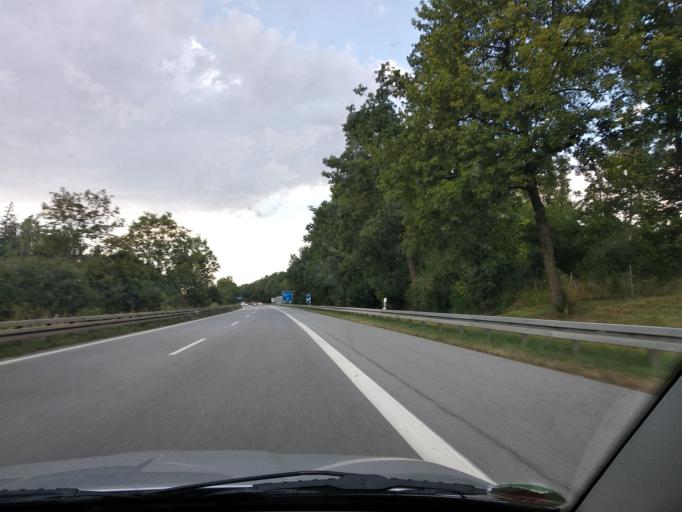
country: DE
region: Bavaria
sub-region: Upper Bavaria
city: Unterhaching
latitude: 48.0751
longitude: 11.5982
